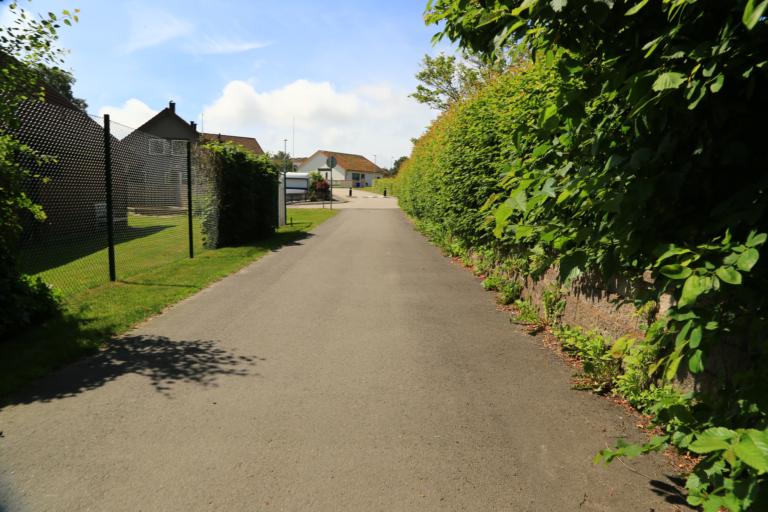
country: SE
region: Halland
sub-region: Varbergs Kommun
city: Traslovslage
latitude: 57.1053
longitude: 12.2936
